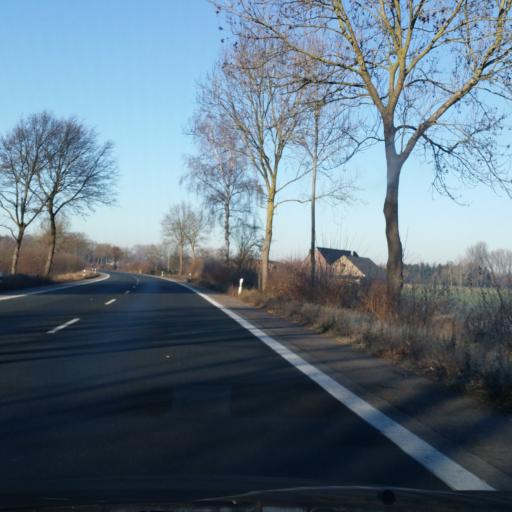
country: DE
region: North Rhine-Westphalia
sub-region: Regierungsbezirk Munster
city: Isselburg
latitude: 51.8172
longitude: 6.4690
